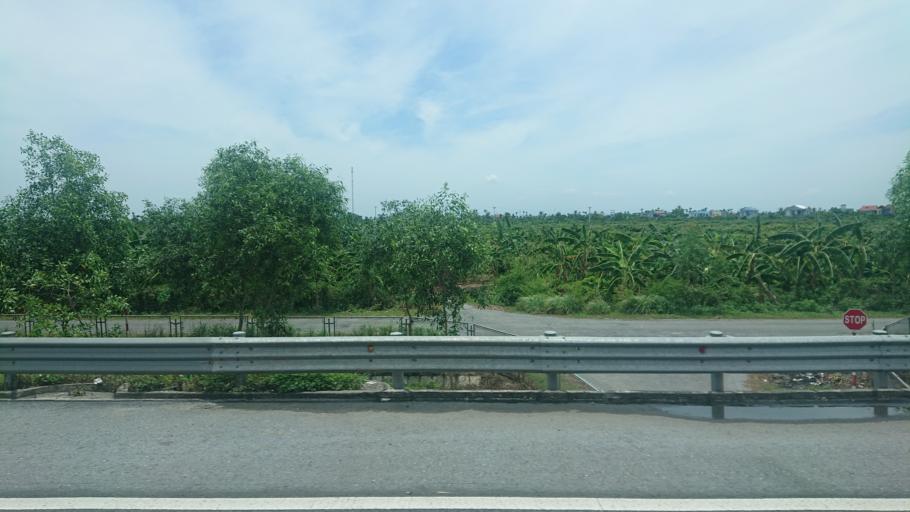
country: VN
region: Hai Duong
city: Tu Ky
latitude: 20.8254
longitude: 106.4640
